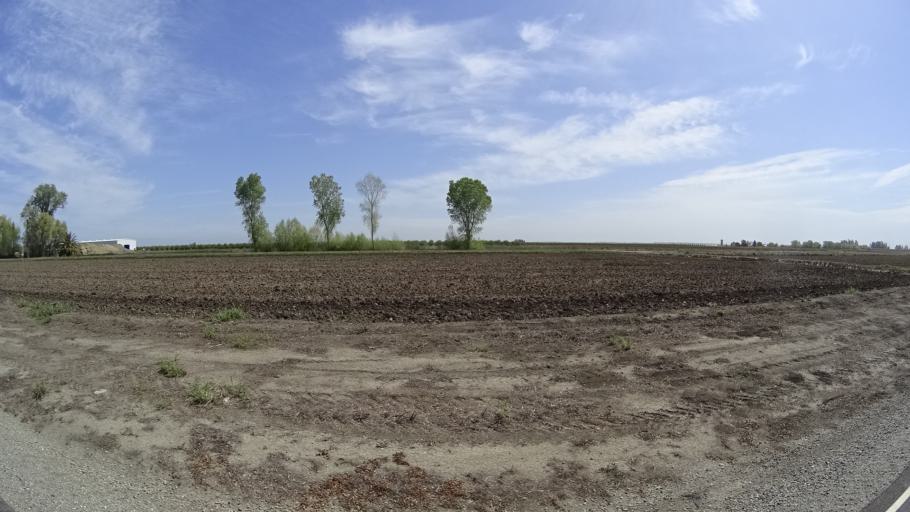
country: US
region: California
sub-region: Glenn County
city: Hamilton City
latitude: 39.6129
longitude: -122.0652
